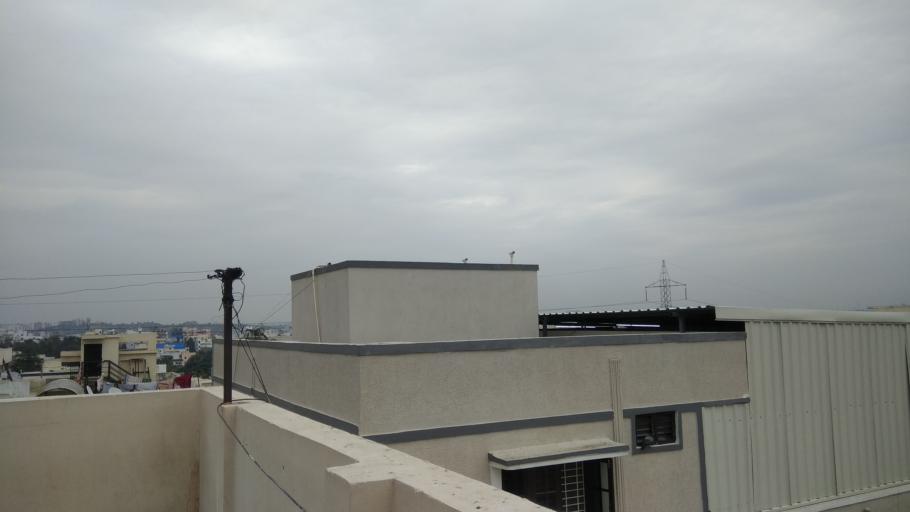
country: IN
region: Telangana
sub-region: Rangareddi
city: Kukatpalli
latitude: 17.4987
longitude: 78.3962
